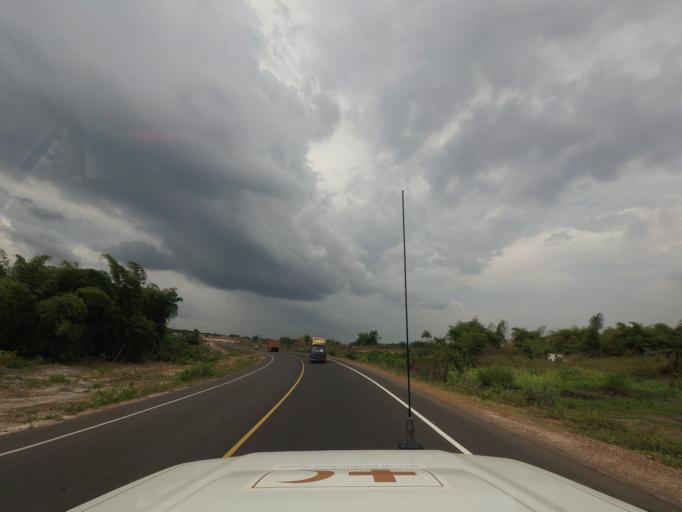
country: LR
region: Margibi
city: Kakata
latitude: 6.5242
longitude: -10.3754
